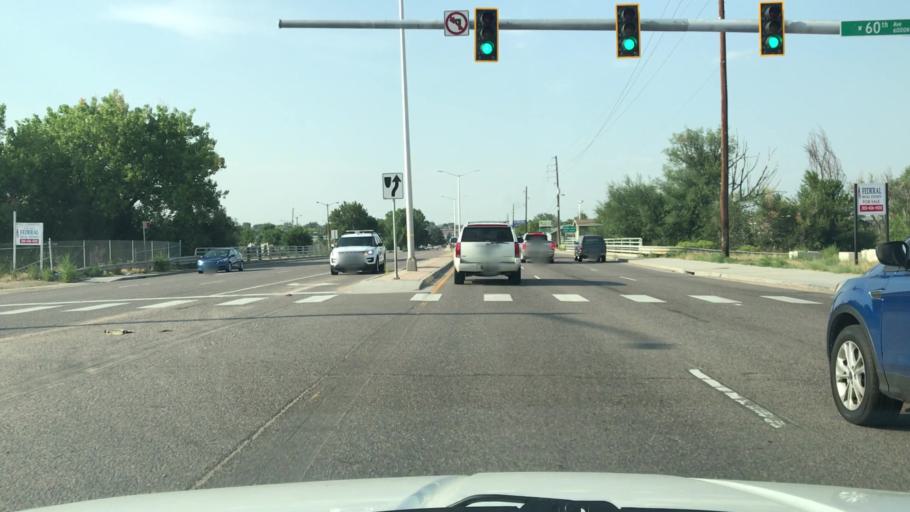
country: US
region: Colorado
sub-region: Adams County
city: Berkley
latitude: 39.8044
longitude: -105.0252
